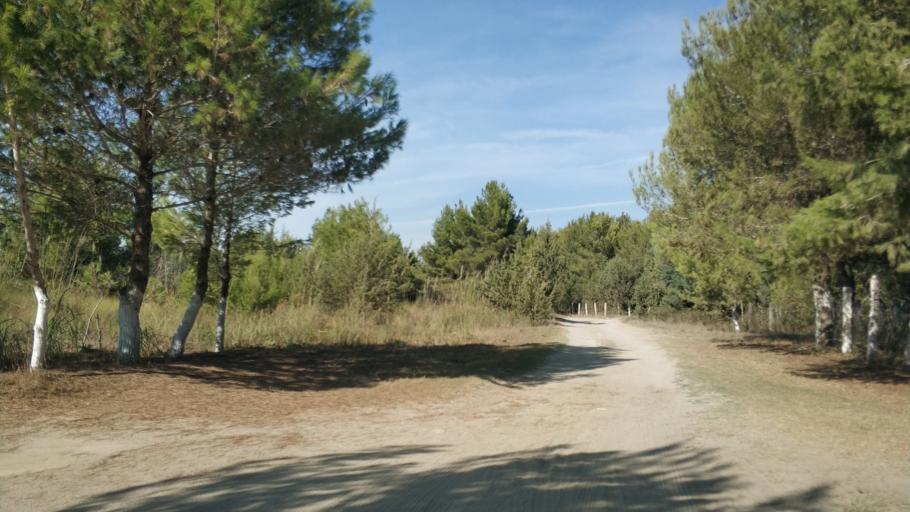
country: AL
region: Fier
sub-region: Rrethi i Lushnjes
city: Divjake
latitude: 40.9616
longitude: 19.4761
